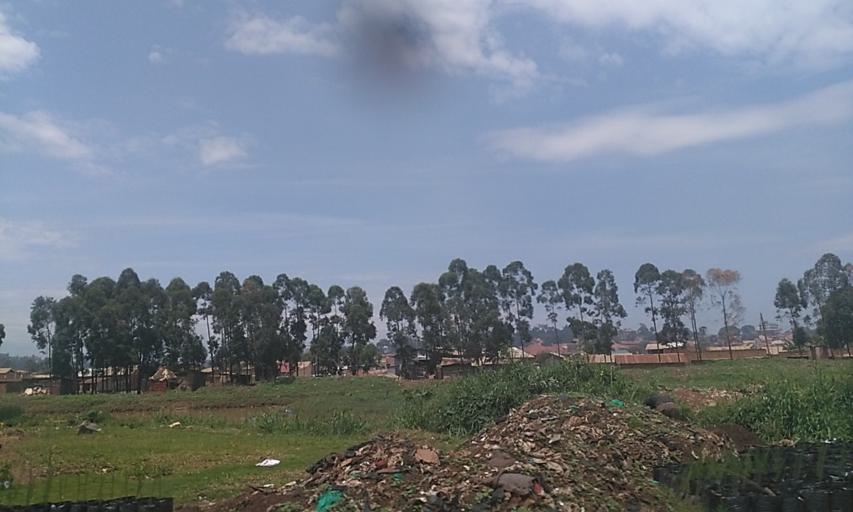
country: UG
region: Central Region
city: Kampala Central Division
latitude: 0.3474
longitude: 32.5550
